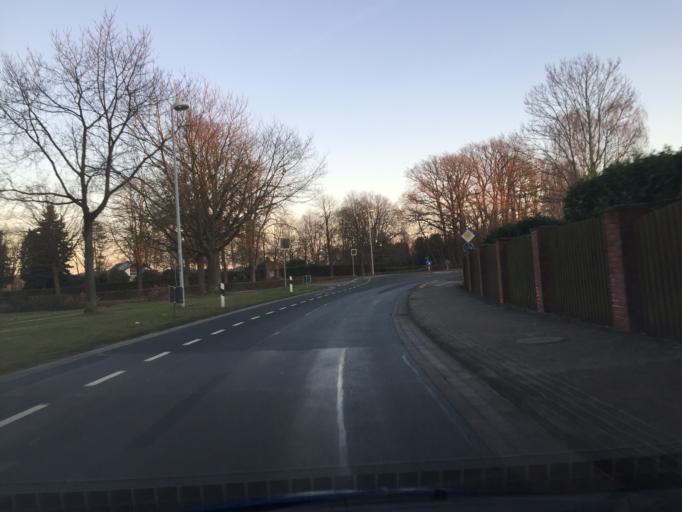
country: DE
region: Lower Saxony
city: Burgdorf
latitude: 52.4667
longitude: 9.9824
